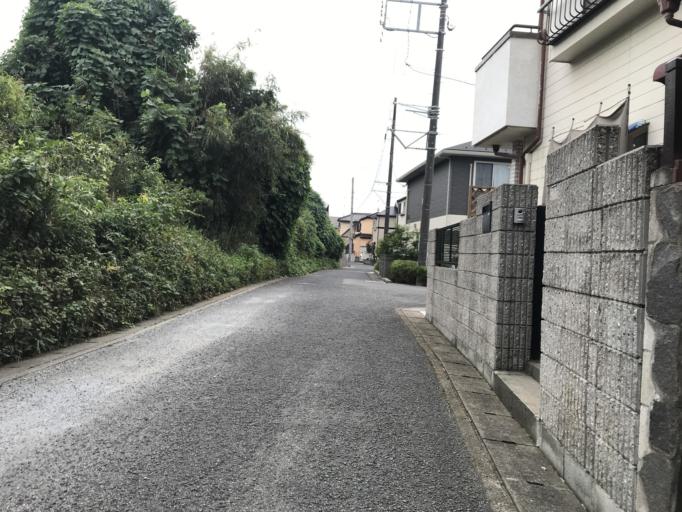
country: JP
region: Saitama
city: Shiraoka
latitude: 36.0091
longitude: 139.6562
